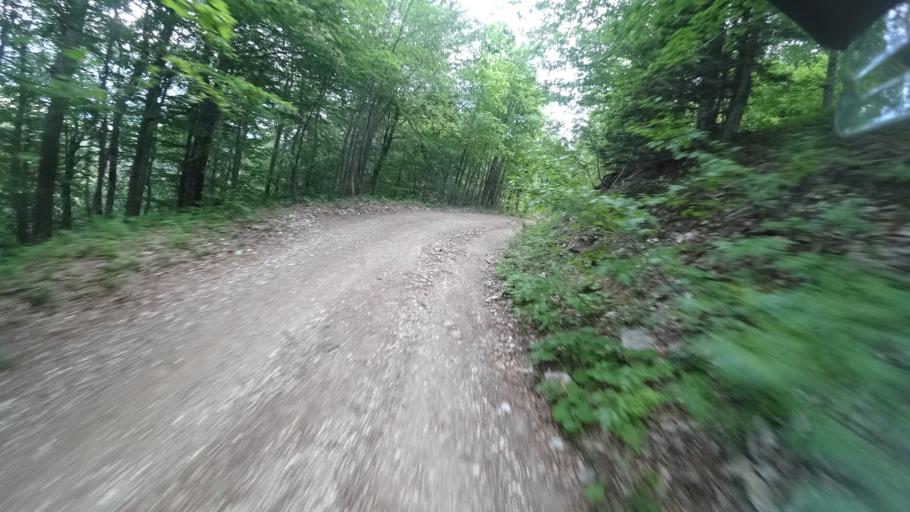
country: HR
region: Licko-Senjska
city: Gospic
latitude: 44.4640
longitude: 15.2978
